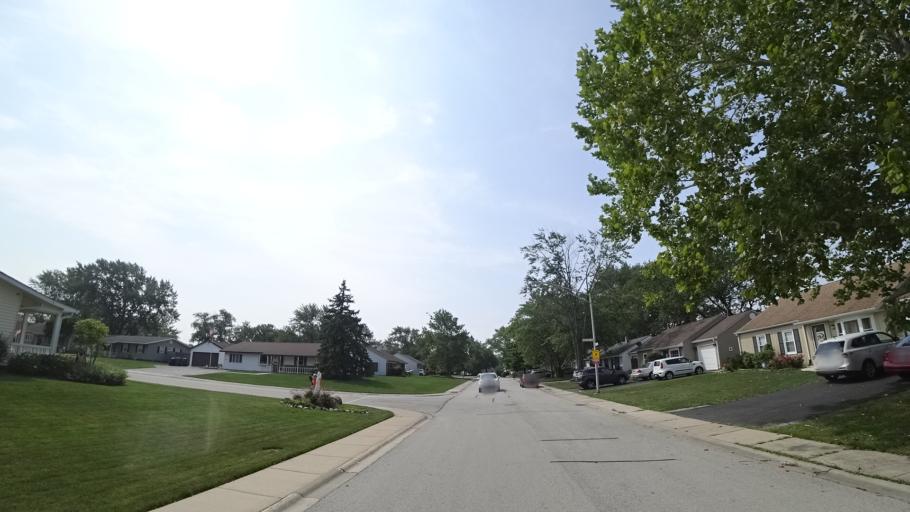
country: US
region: Illinois
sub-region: Cook County
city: Orland Park
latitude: 41.6168
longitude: -87.8709
